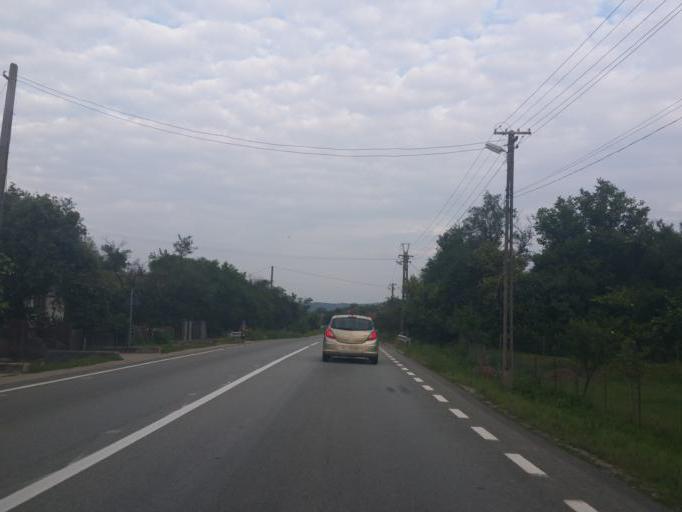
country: RO
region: Salaj
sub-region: Comuna Sanmihaiu Almasului
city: Sanmihaiu Almasului
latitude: 46.9586
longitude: 23.3331
